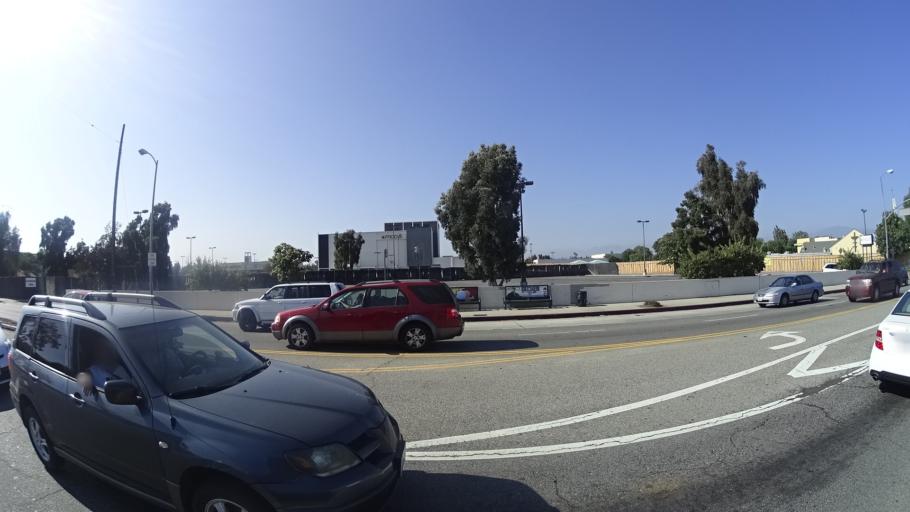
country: US
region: California
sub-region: Los Angeles County
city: North Hollywood
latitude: 34.1793
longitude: -118.3940
